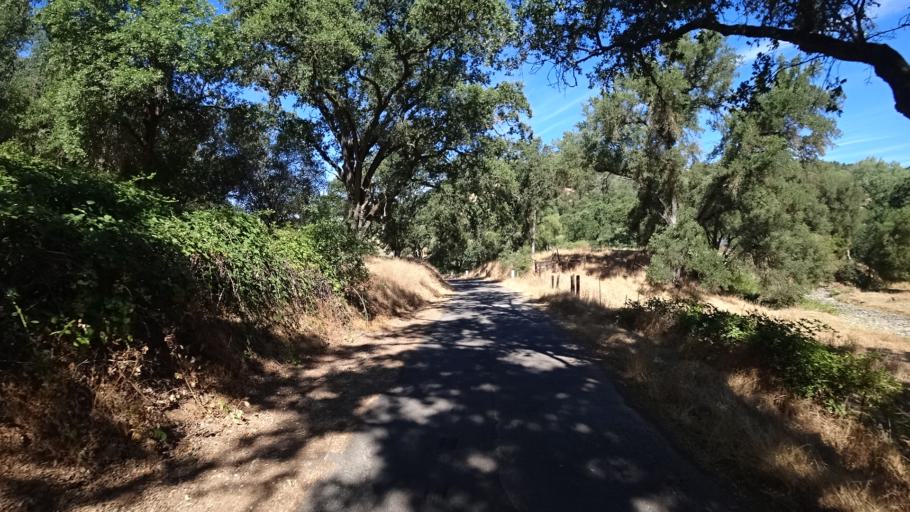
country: US
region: California
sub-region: Calaveras County
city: Angels Camp
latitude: 38.1475
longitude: -120.5735
